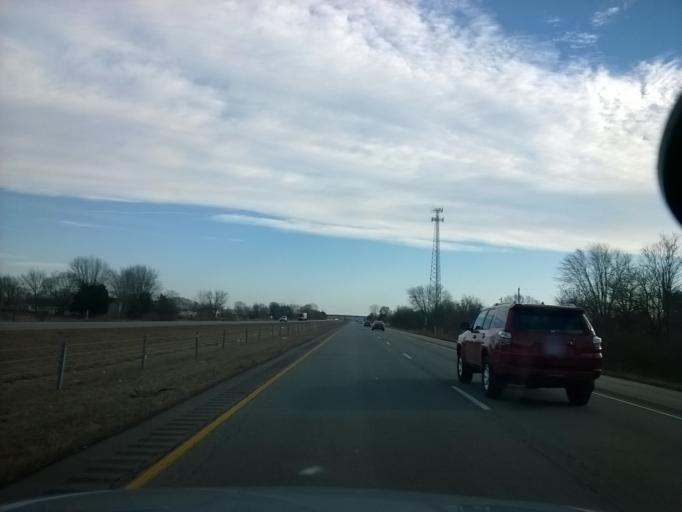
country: US
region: Indiana
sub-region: Johnson County
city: Edinburgh
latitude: 39.4257
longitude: -85.9725
